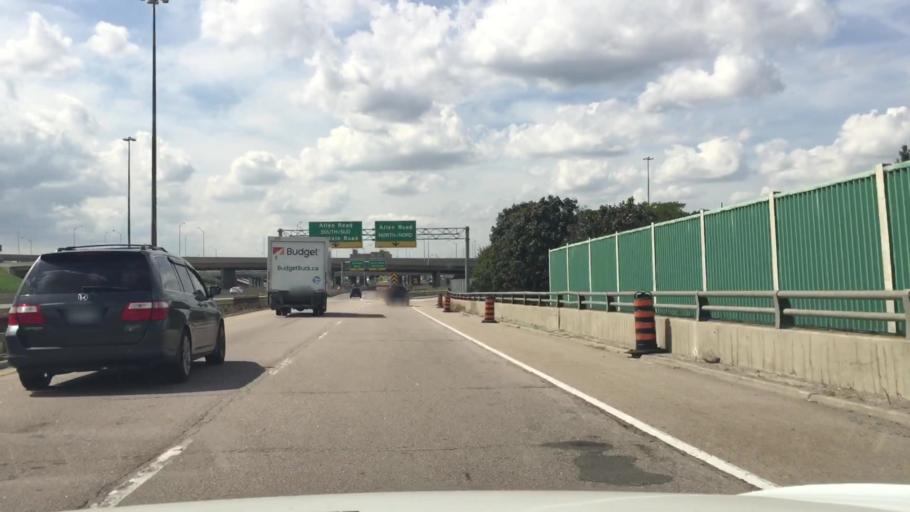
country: CA
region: Ontario
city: Toronto
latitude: 43.7319
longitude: -79.4437
